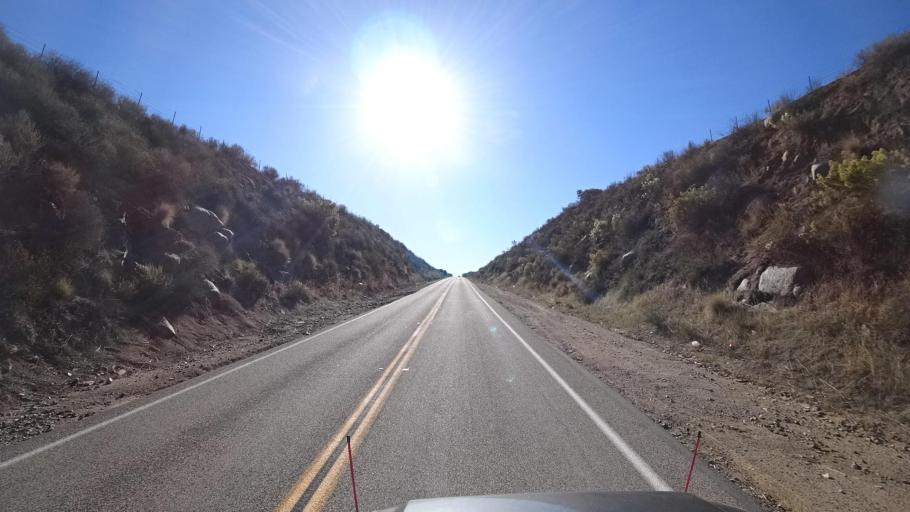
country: US
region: California
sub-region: San Diego County
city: Jamul
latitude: 32.6706
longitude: -116.8027
